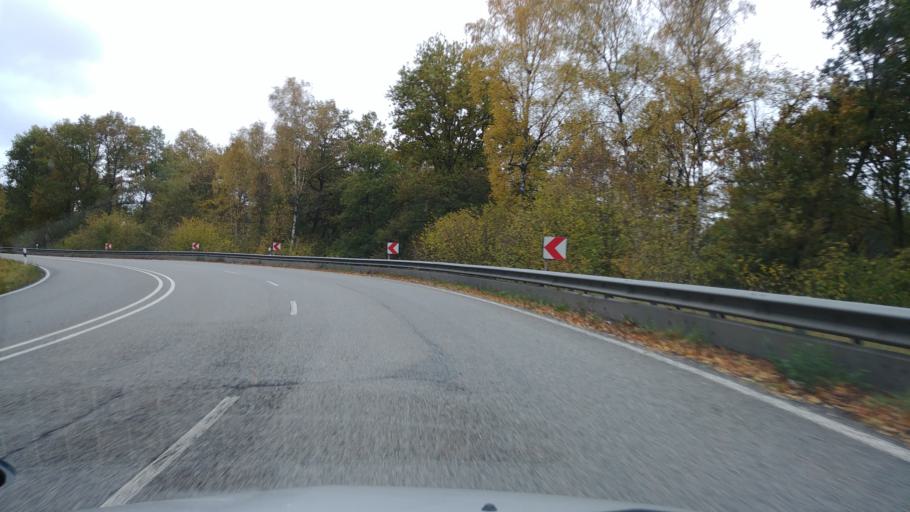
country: DE
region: Rheinland-Pfalz
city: Etgert
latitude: 49.7808
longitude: 7.0373
